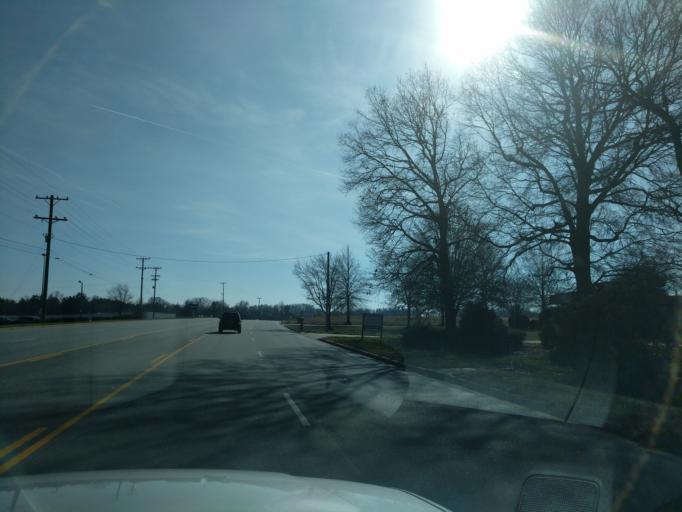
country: US
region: South Carolina
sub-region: Spartanburg County
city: Duncan
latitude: 34.8698
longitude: -82.1426
